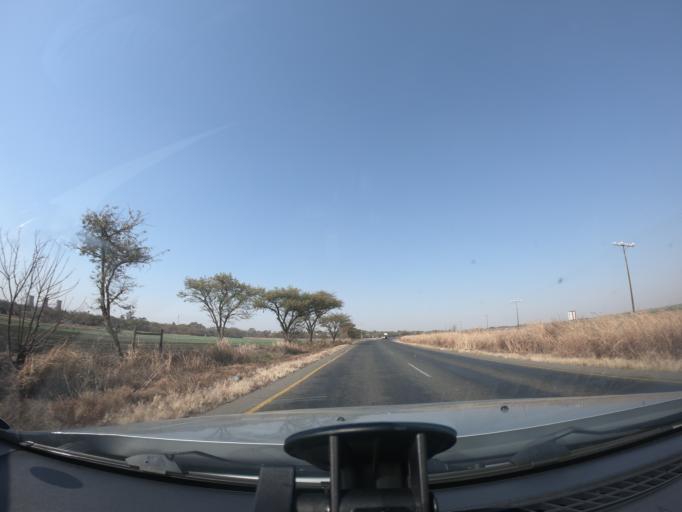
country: ZA
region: KwaZulu-Natal
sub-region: uThukela District Municipality
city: Ladysmith
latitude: -28.7345
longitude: 29.8154
